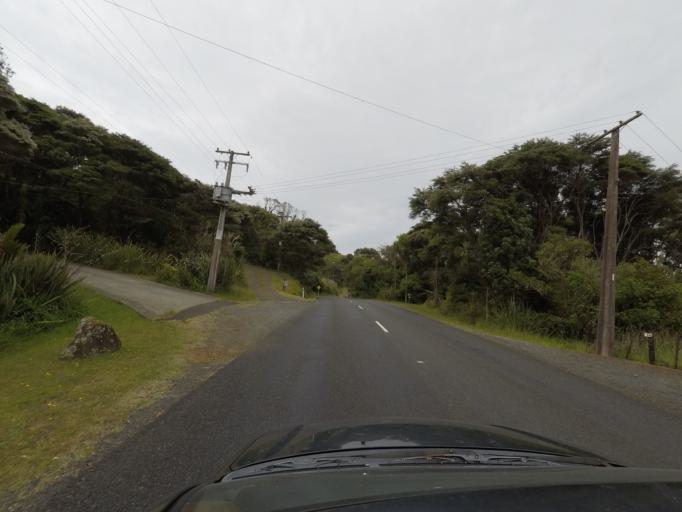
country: NZ
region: Waikato
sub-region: Waikato District
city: Raglan
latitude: -37.8265
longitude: 174.8163
